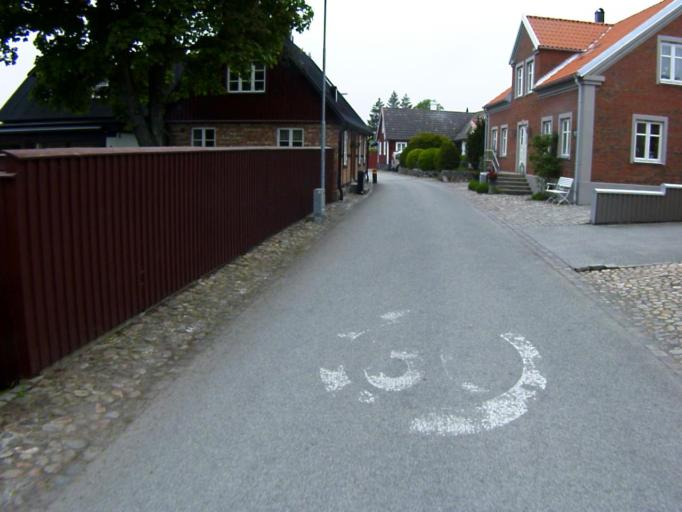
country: SE
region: Skane
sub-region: Kristianstads Kommun
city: Ahus
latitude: 55.9206
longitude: 14.2899
